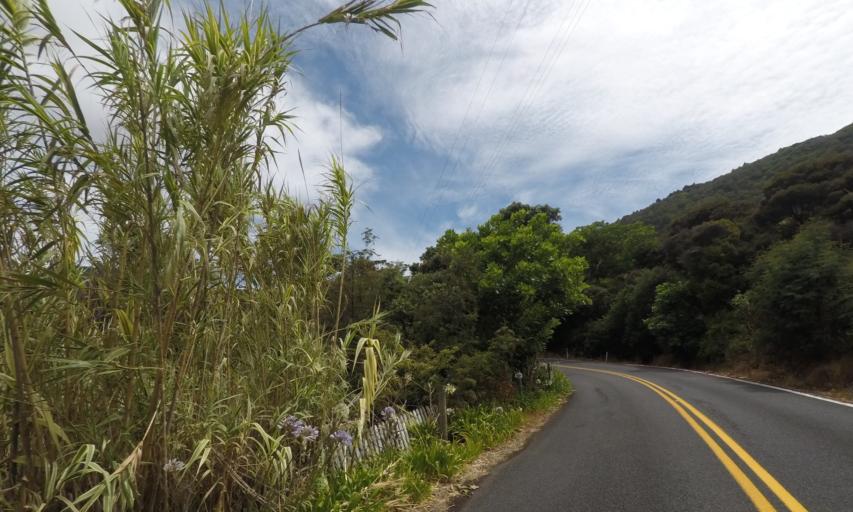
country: NZ
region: Northland
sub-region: Whangarei
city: Ruakaka
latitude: -35.8327
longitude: 174.5316
